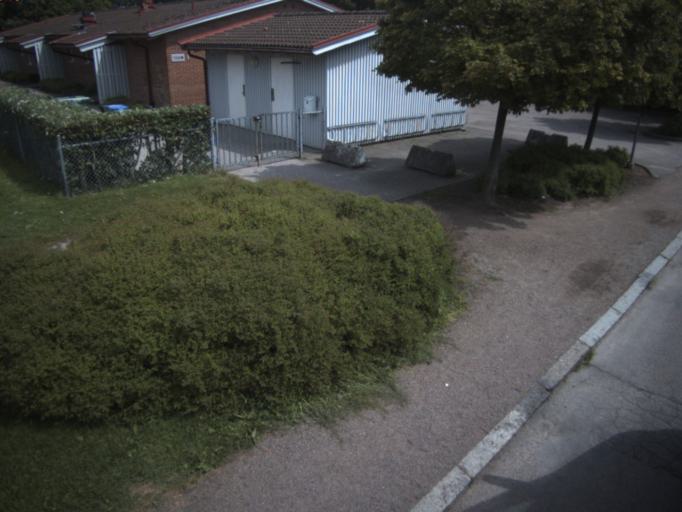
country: SE
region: Skane
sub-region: Helsingborg
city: Helsingborg
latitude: 56.0435
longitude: 12.7213
